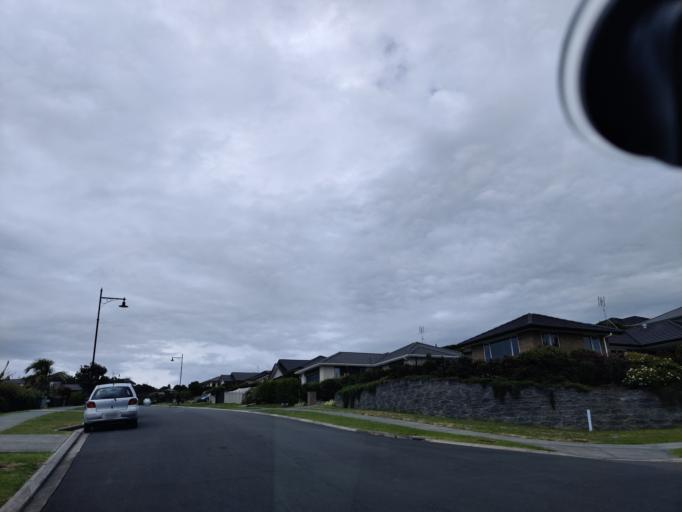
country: NZ
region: Auckland
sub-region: Auckland
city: Rothesay Bay
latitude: -36.5682
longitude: 174.6858
